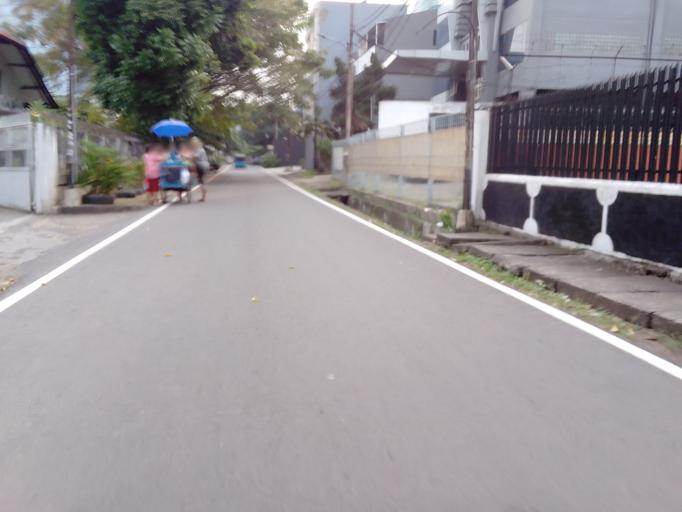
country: ID
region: Jakarta Raya
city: Jakarta
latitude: -6.1777
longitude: 106.8166
